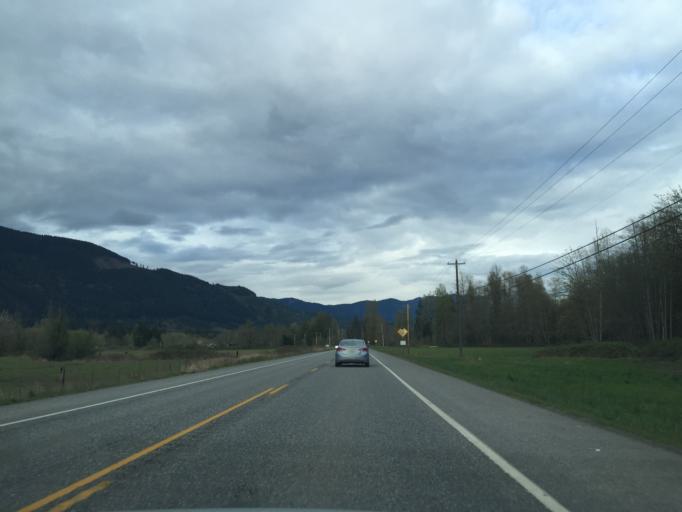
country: US
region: Washington
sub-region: Snohomish County
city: Arlington Heights
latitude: 48.2687
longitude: -122.0090
